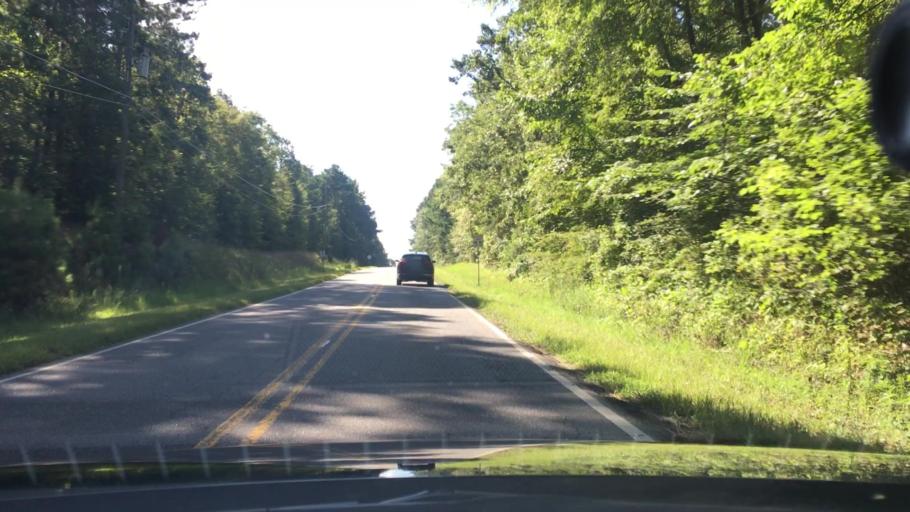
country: US
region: Georgia
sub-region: Putnam County
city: Jefferson
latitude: 33.3992
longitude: -83.2739
